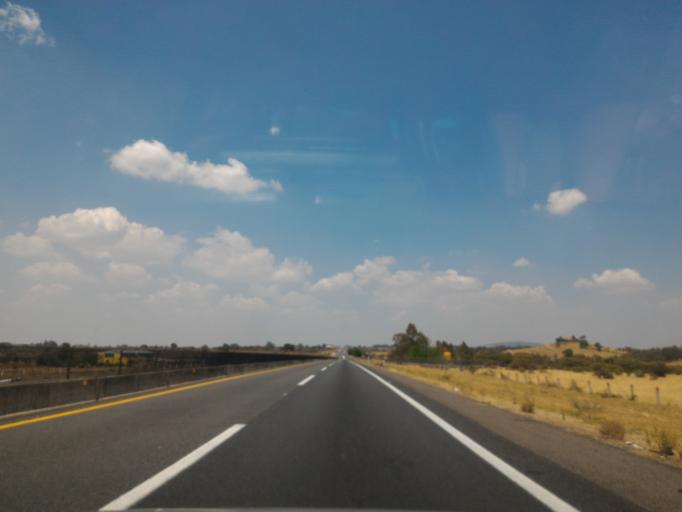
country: MX
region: Jalisco
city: Tepatitlan de Morelos
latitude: 20.8745
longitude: -102.7438
